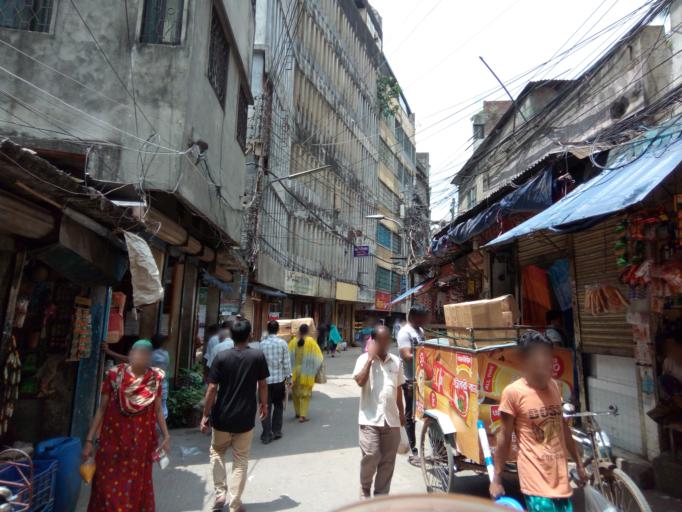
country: BD
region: Dhaka
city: Paltan
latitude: 23.7332
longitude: 90.4175
